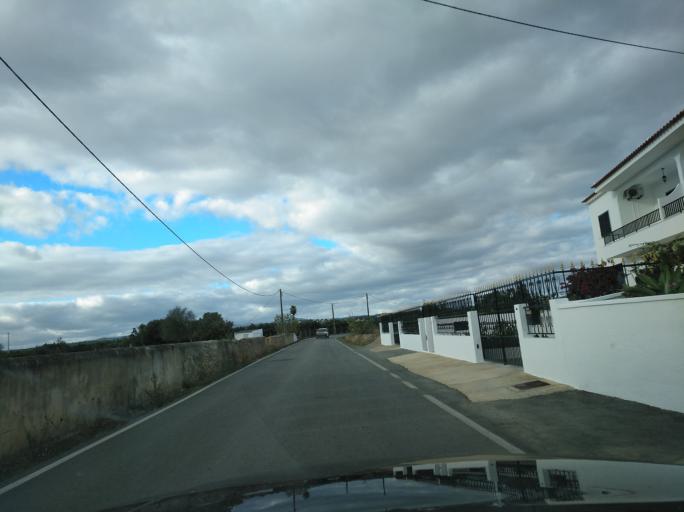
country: PT
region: Faro
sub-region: Tavira
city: Luz
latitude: 37.1018
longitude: -7.7083
